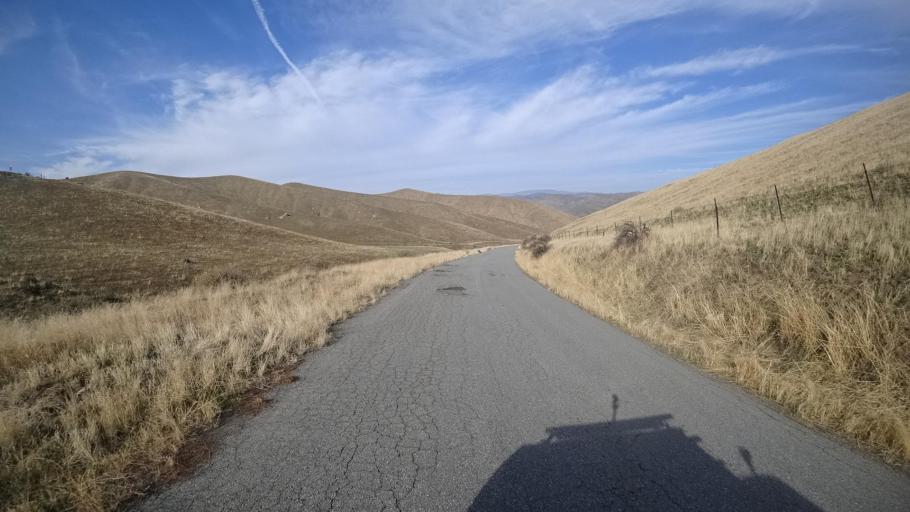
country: US
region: California
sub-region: Kern County
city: Bear Valley Springs
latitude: 35.2813
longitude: -118.6735
